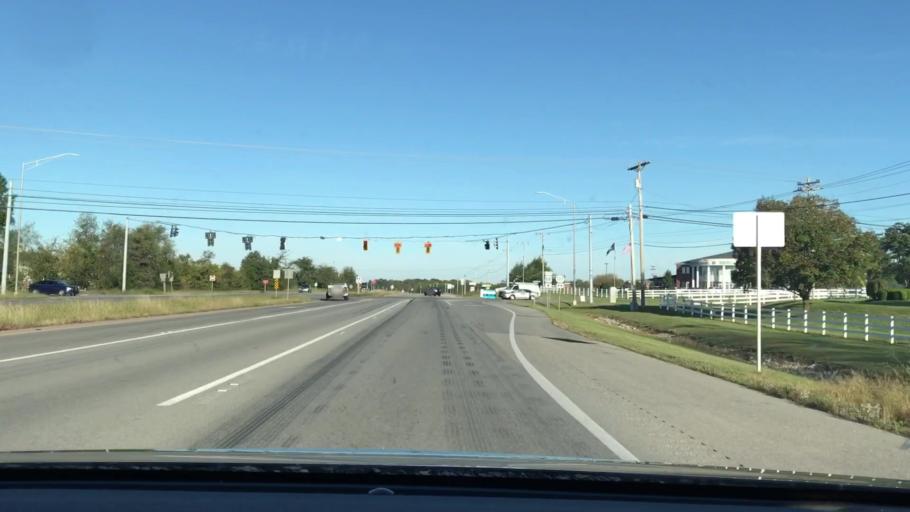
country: US
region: Kentucky
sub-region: Christian County
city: Hopkinsville
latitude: 36.8213
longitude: -87.5039
